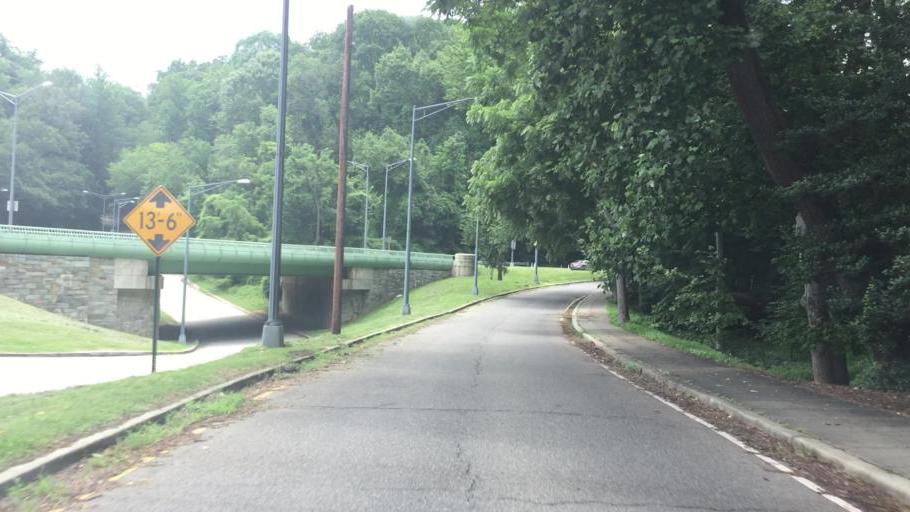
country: US
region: Washington, D.C.
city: Washington, D.C.
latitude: 38.9340
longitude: -77.0510
